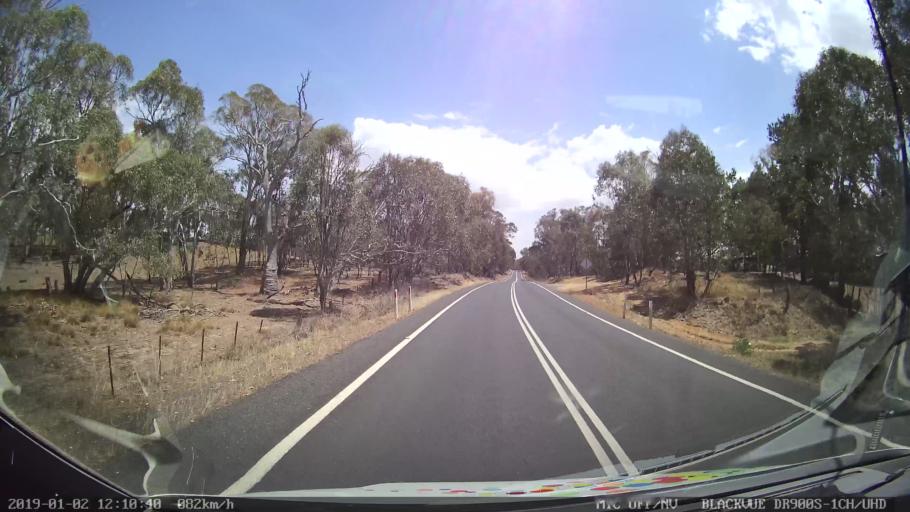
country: AU
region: New South Wales
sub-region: Young
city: Young
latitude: -34.4579
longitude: 148.2615
